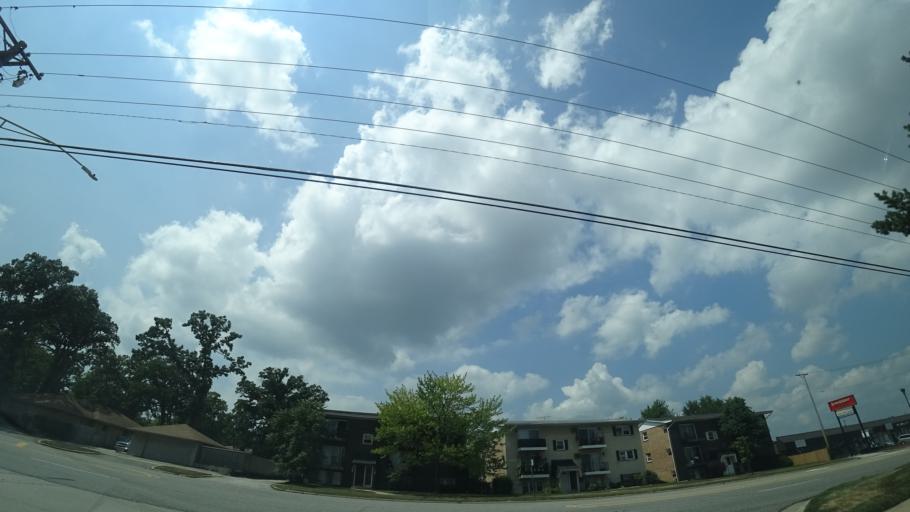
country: US
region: Illinois
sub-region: Cook County
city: Worth
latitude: 41.6953
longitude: -87.7975
